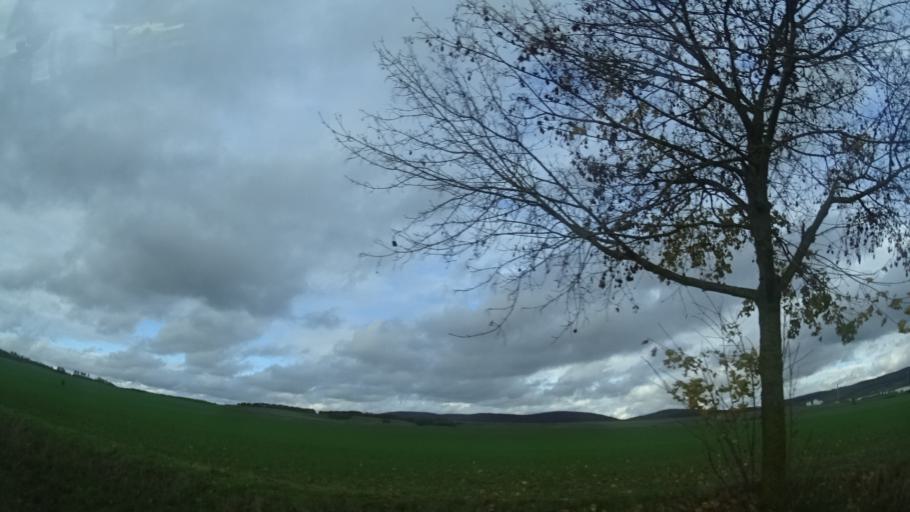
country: DE
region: Thuringia
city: Romhild
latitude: 50.3937
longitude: 10.5248
